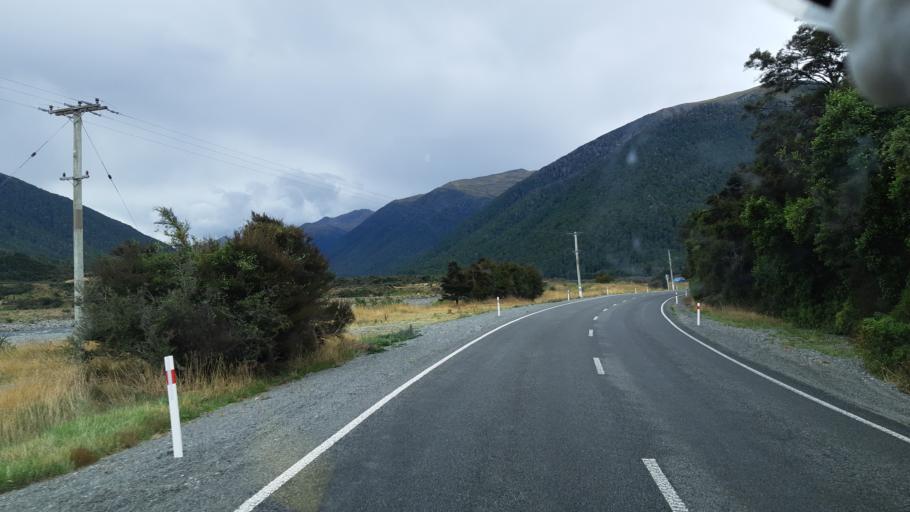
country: NZ
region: Canterbury
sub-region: Hurunui District
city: Amberley
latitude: -42.5560
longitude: 172.3489
